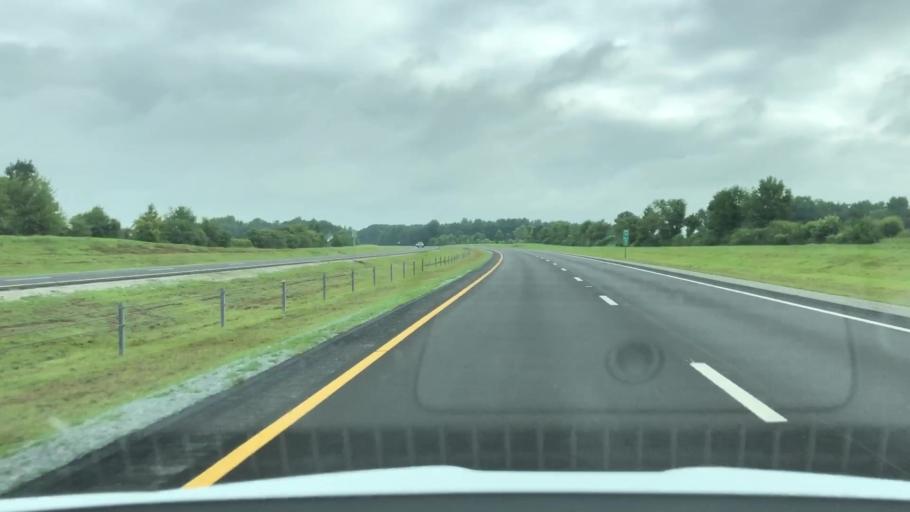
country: US
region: North Carolina
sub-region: Wayne County
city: Fremont
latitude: 35.5176
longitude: -77.9918
